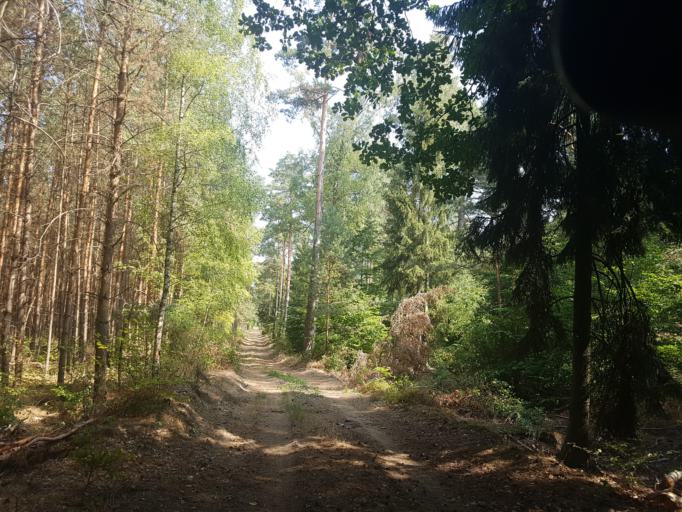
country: DE
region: Brandenburg
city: Gorzke
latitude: 52.0899
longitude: 12.3221
